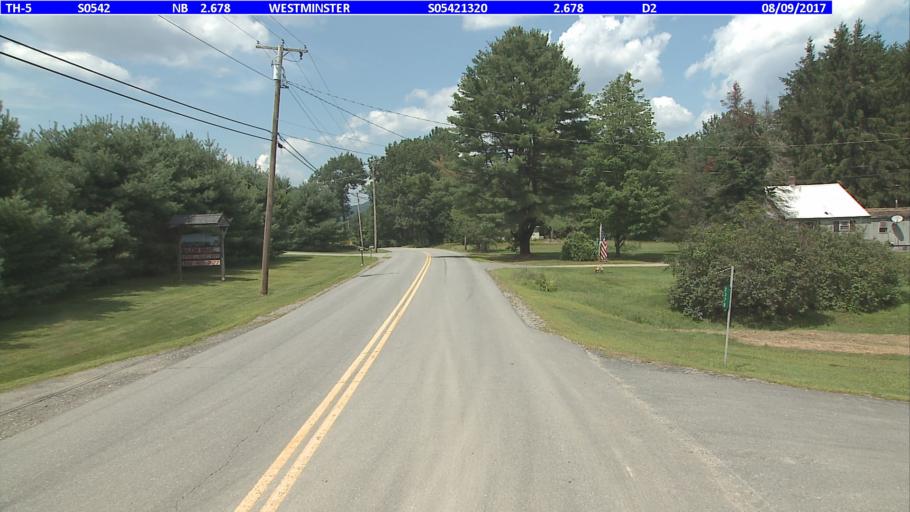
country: US
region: Vermont
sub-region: Windham County
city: Bellows Falls
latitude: 43.1205
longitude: -72.4665
